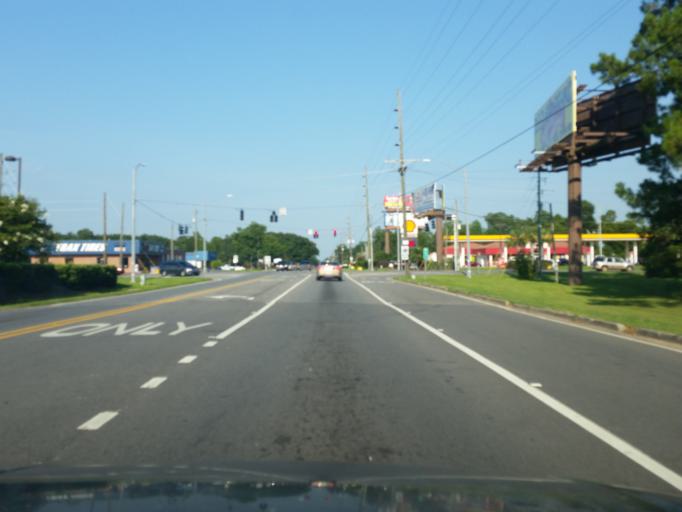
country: US
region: Alabama
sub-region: Baldwin County
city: Foley
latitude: 30.4068
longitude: -87.6485
